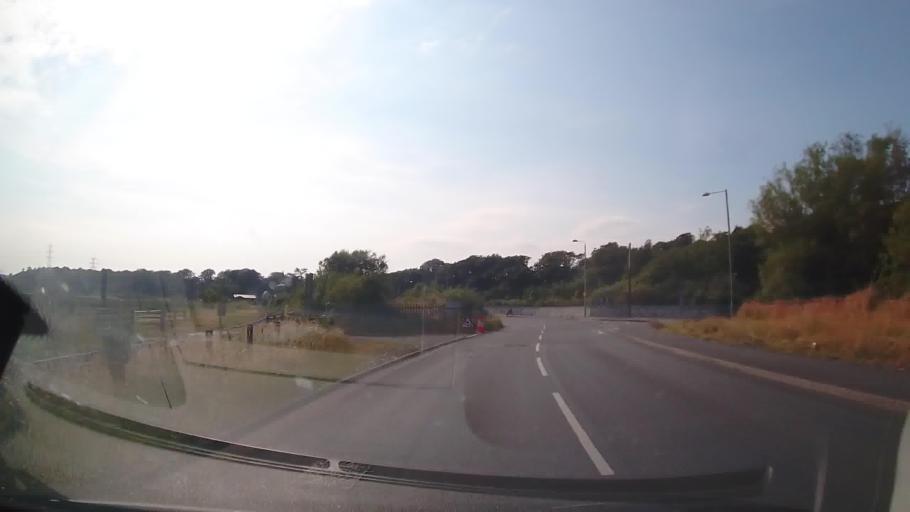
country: GB
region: Wales
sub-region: Gwynedd
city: Penrhyndeudraeth
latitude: 52.9296
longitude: -4.0599
